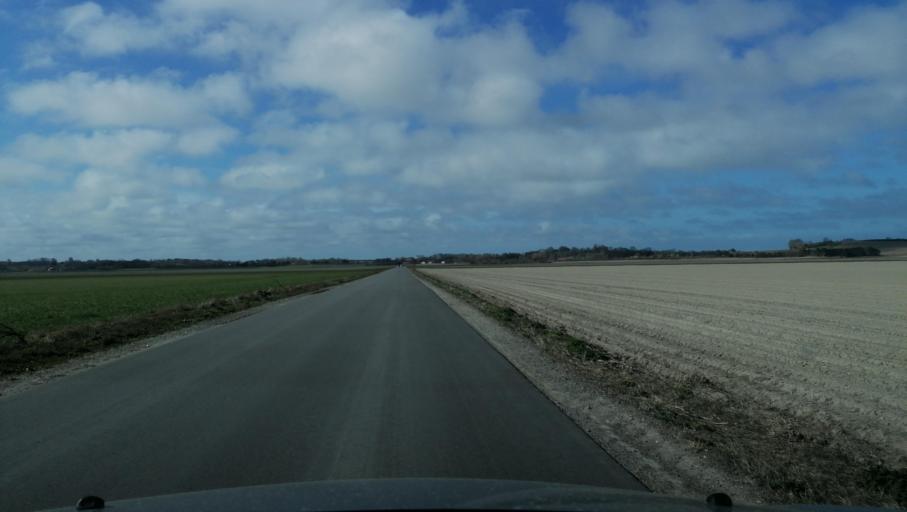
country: DK
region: Zealand
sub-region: Odsherred Kommune
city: Horve
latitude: 55.7843
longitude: 11.4424
